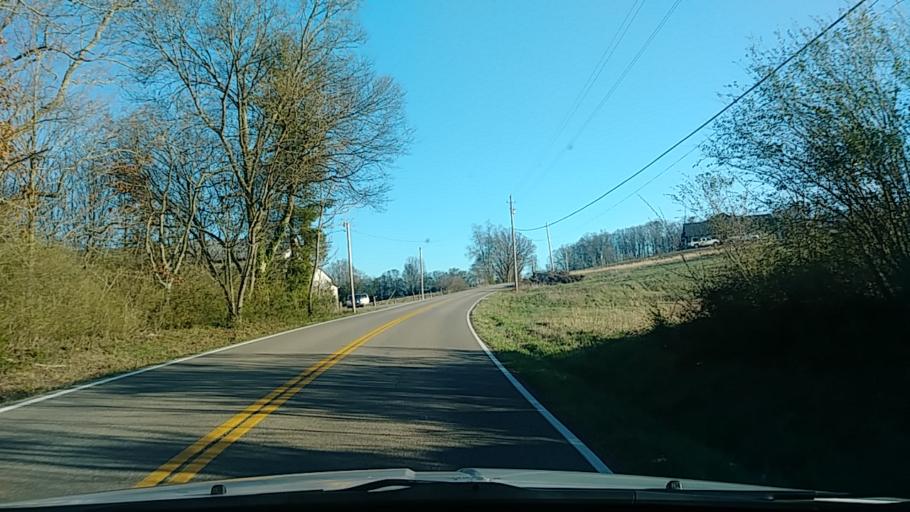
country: US
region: Tennessee
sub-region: Hamblen County
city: Morristown
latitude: 36.2021
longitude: -83.4028
